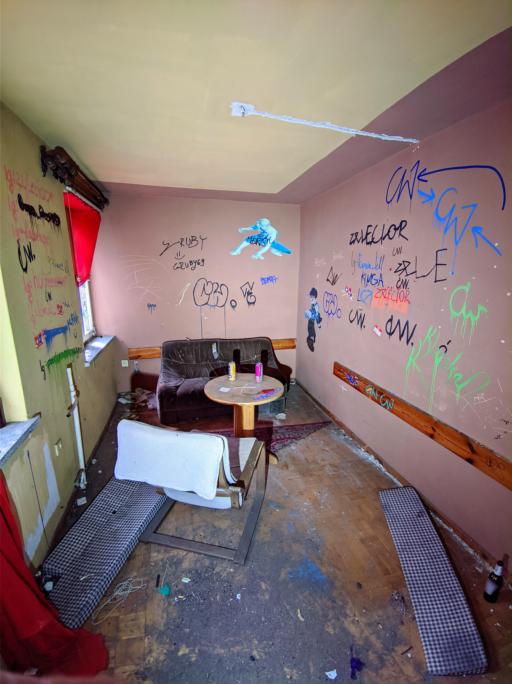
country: PL
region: Lubusz
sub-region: Powiat swiebodzinski
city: Lubrza
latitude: 52.3116
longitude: 15.4255
